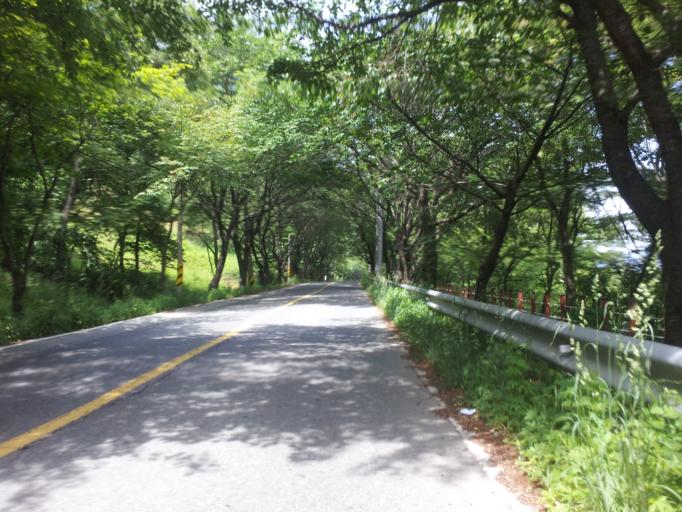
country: KR
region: Daejeon
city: Sintansin
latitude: 36.4331
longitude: 127.4687
